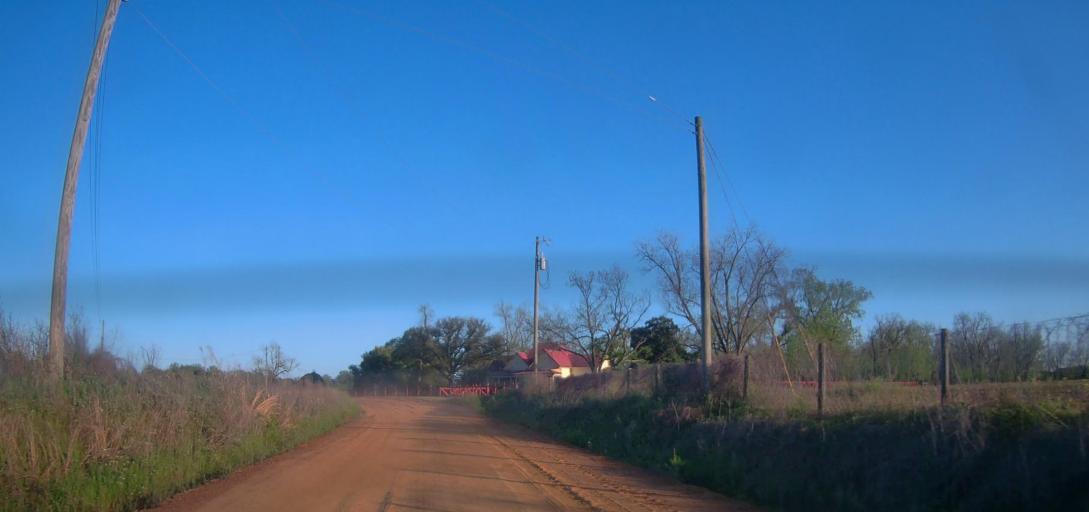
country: US
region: Georgia
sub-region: Irwin County
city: Ocilla
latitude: 31.6437
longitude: -83.2214
